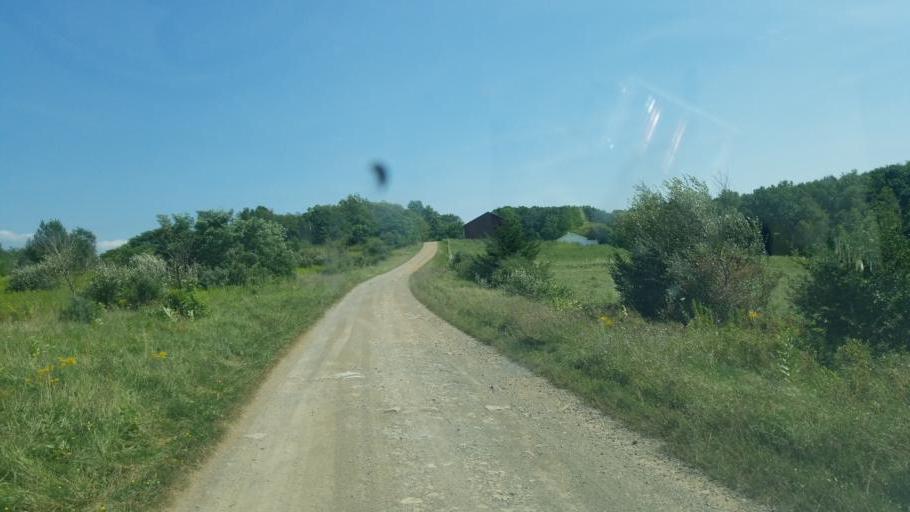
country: US
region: Pennsylvania
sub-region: Clarion County
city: Knox
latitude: 41.1016
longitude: -79.5262
